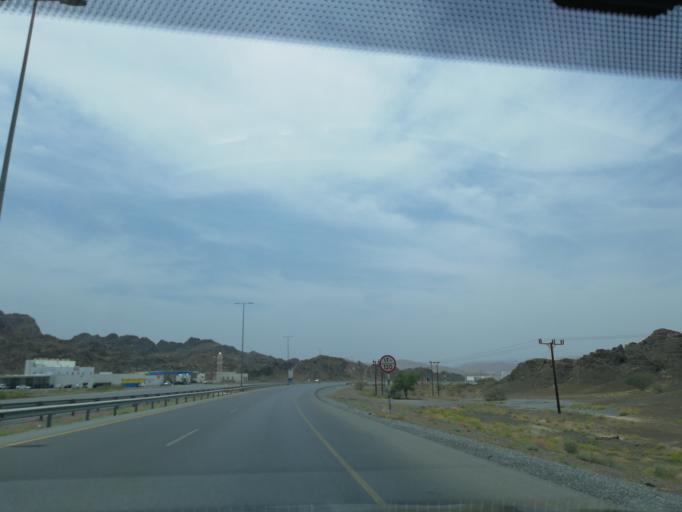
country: OM
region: Muhafazat ad Dakhiliyah
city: Izki
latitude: 22.9176
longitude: 57.7782
